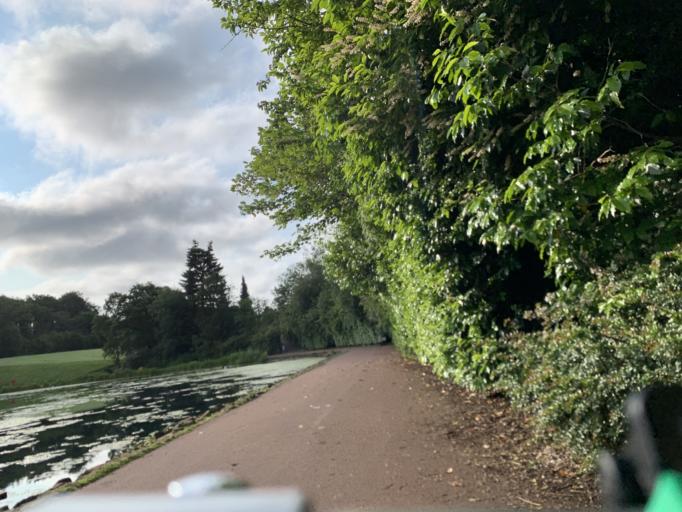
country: GB
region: Scotland
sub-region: East Renfrewshire
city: Giffnock
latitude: 55.7915
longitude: -4.3150
